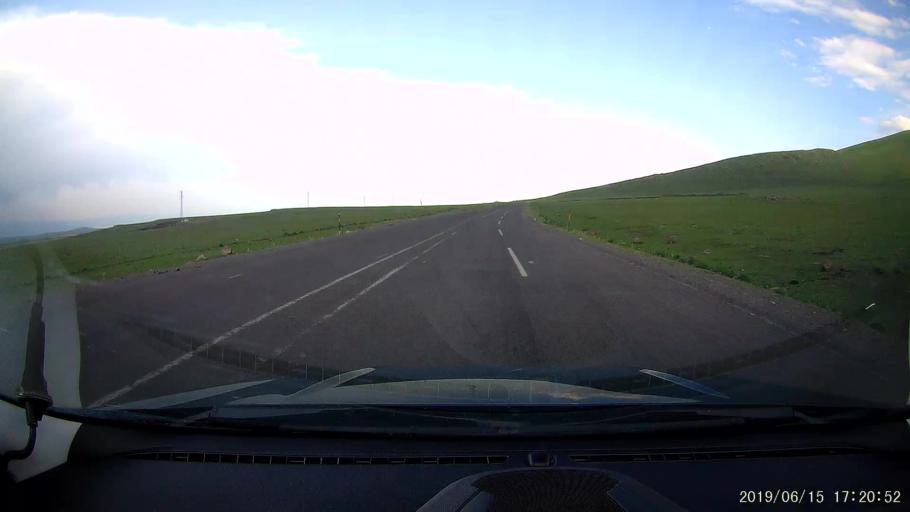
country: TR
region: Kars
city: Basgedikler
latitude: 40.6171
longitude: 43.3122
